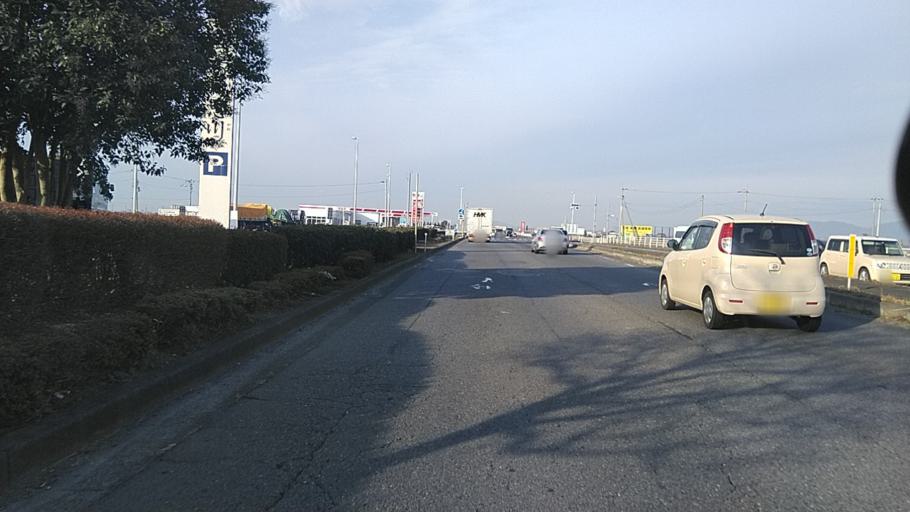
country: JP
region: Tochigi
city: Oyama
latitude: 36.3090
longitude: 139.7608
